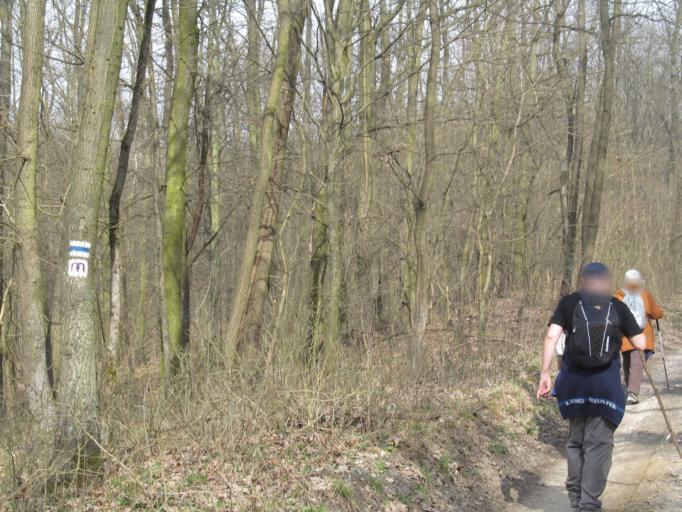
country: HU
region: Komarom-Esztergom
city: Tatabanya
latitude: 47.5880
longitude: 18.4521
